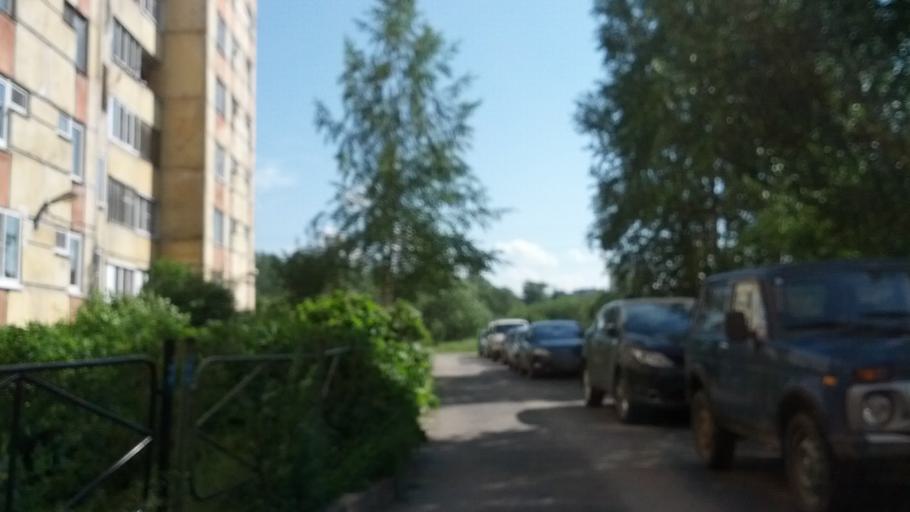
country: RU
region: Leningrad
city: Rybatskoye
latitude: 59.8896
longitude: 30.4842
